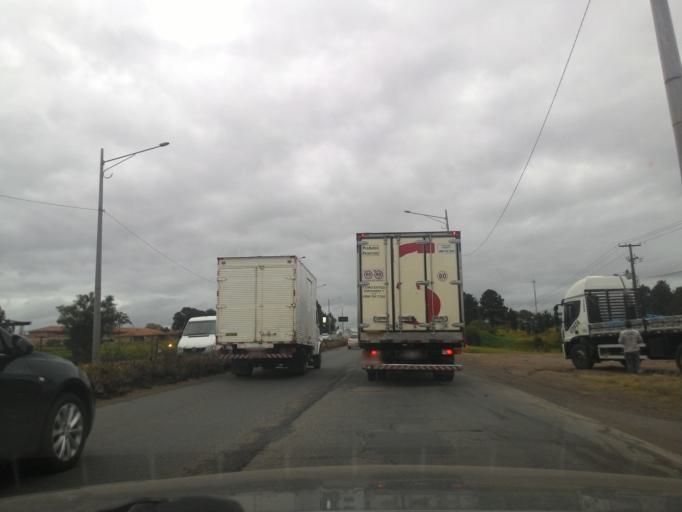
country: BR
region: Parana
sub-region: Sao Jose Dos Pinhais
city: Sao Jose dos Pinhais
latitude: -25.5339
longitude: -49.3006
